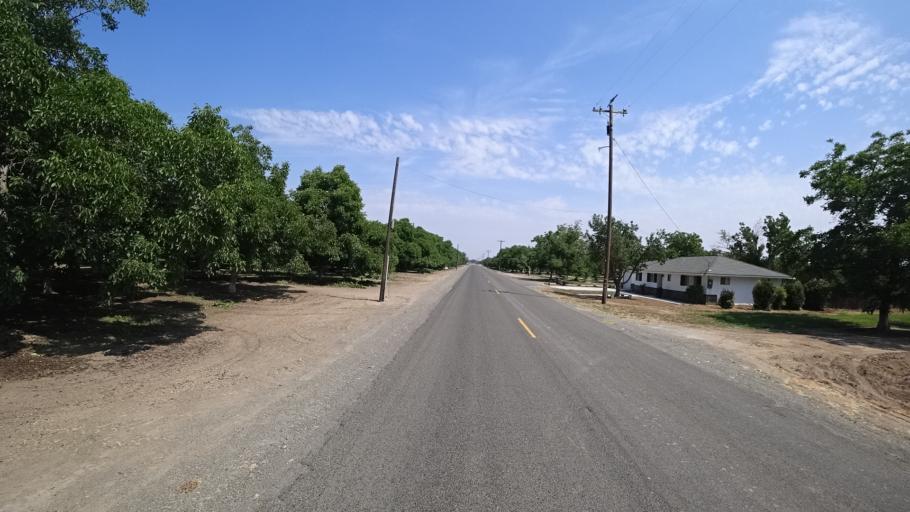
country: US
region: California
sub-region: Fresno County
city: Laton
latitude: 36.3968
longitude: -119.7450
